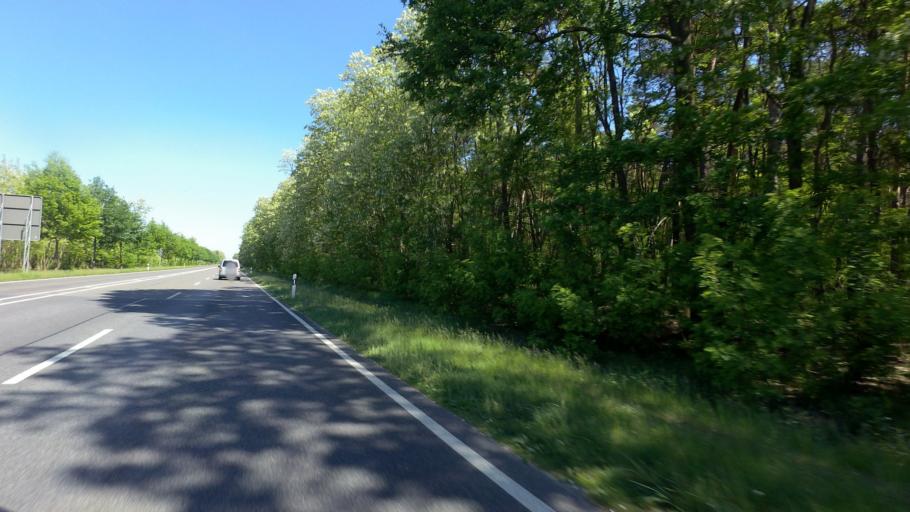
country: DE
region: Brandenburg
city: Spremberg
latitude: 51.6131
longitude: 14.3632
